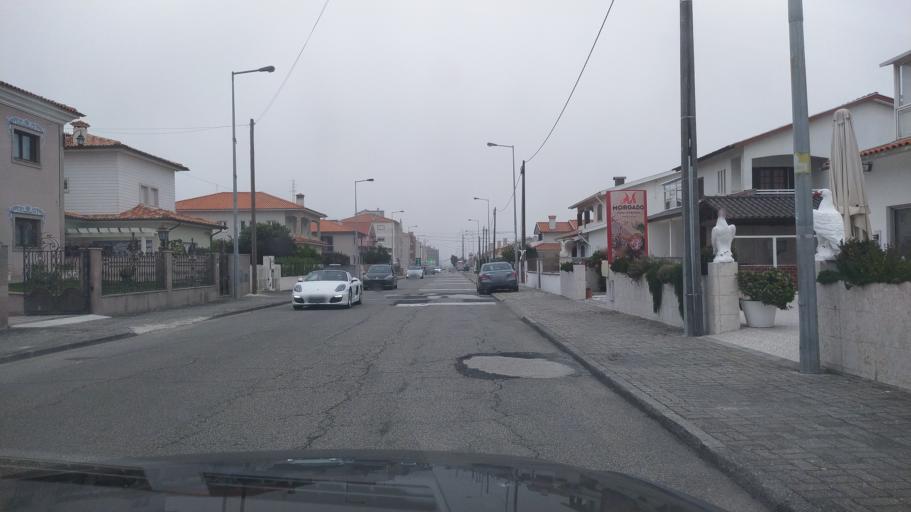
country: PT
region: Aveiro
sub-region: Ilhavo
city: Gafanha da Encarnacao
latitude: 40.5582
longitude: -8.7478
